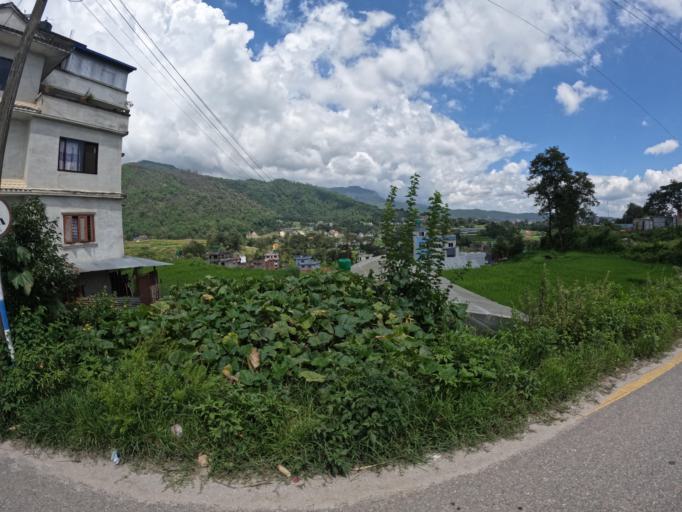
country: NP
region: Central Region
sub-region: Bagmati Zone
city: Kathmandu
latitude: 27.7764
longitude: 85.3272
